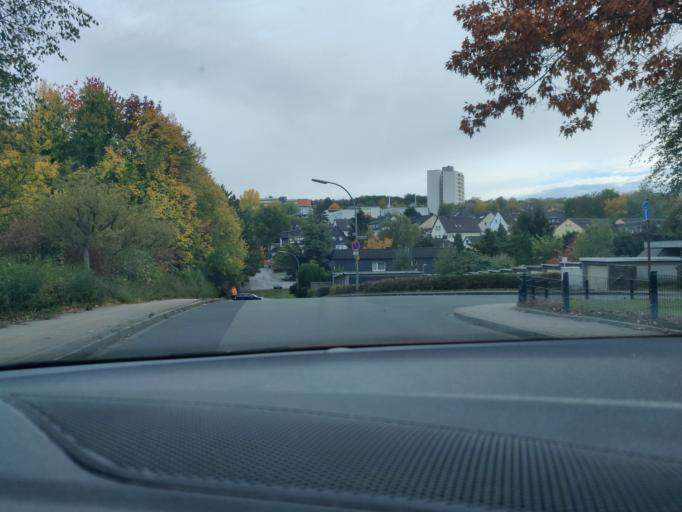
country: DE
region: North Rhine-Westphalia
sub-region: Regierungsbezirk Dusseldorf
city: Velbert
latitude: 51.3417
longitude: 7.0134
